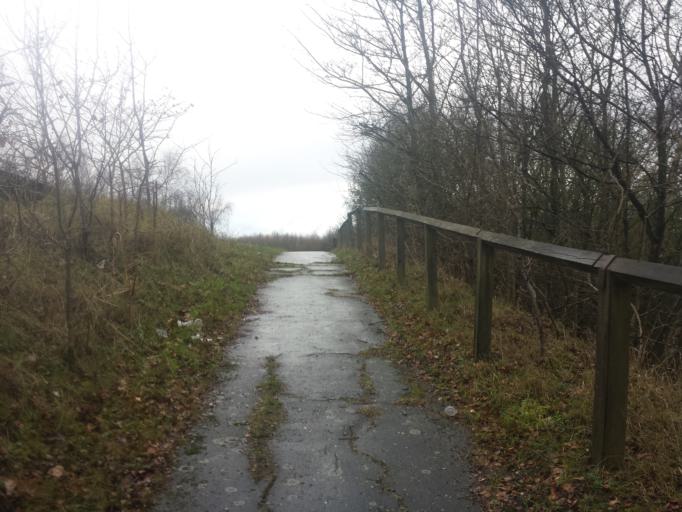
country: GB
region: England
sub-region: Essex
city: Great Bentley
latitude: 51.8844
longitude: 1.0468
